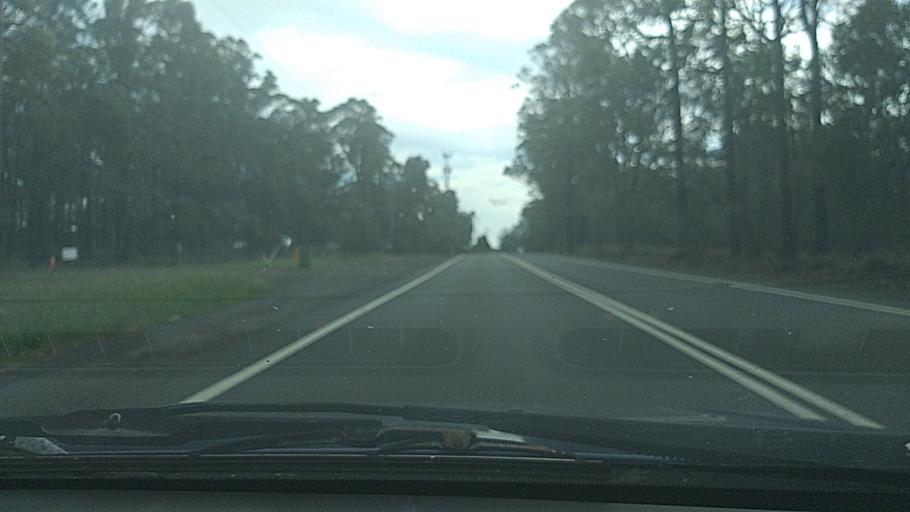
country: AU
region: New South Wales
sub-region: Hawkesbury
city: South Windsor
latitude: -33.6645
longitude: 150.7590
